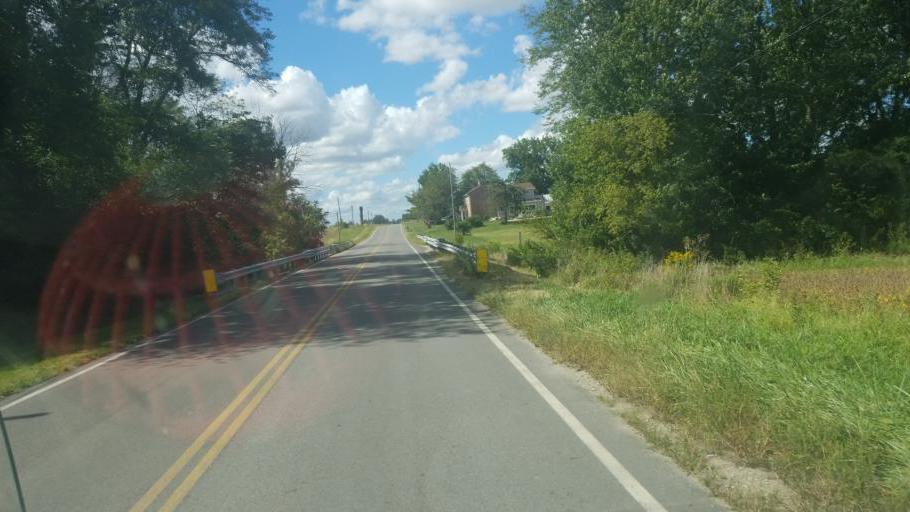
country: US
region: Ohio
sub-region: Union County
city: Marysville
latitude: 40.1836
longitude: -83.4513
